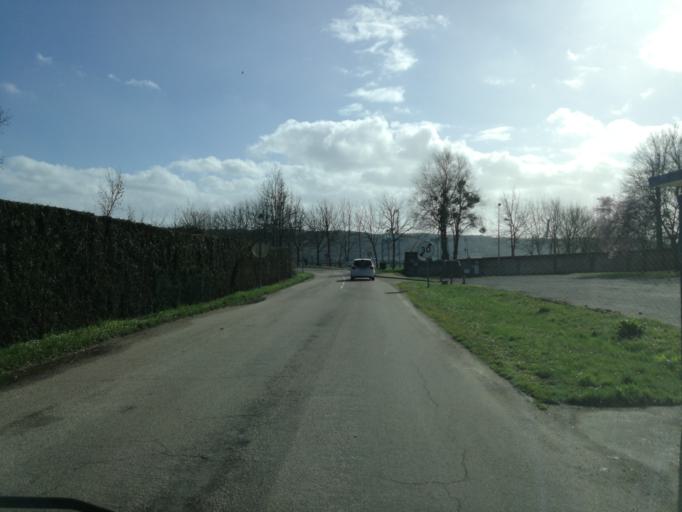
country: FR
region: Haute-Normandie
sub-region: Departement de la Seine-Maritime
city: Grand-Couronne
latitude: 49.3609
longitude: 0.9793
